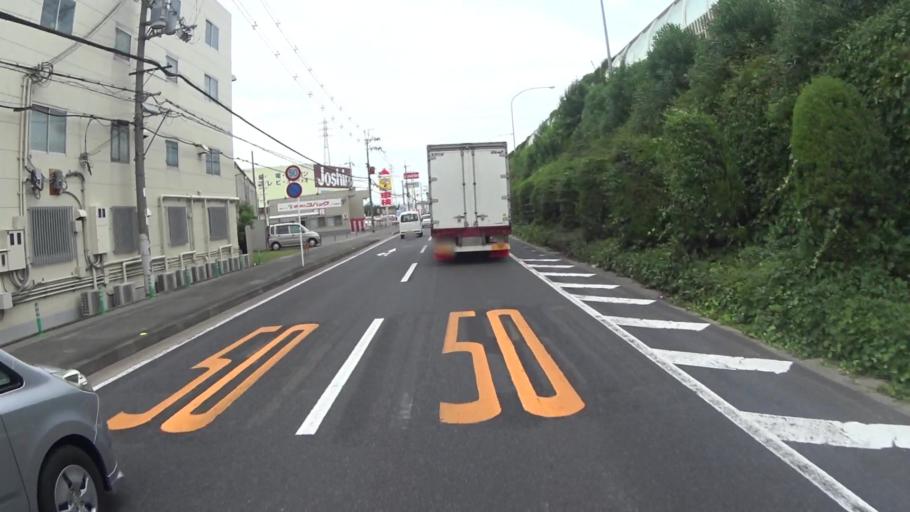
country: JP
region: Kyoto
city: Muko
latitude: 34.9231
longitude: 135.7103
